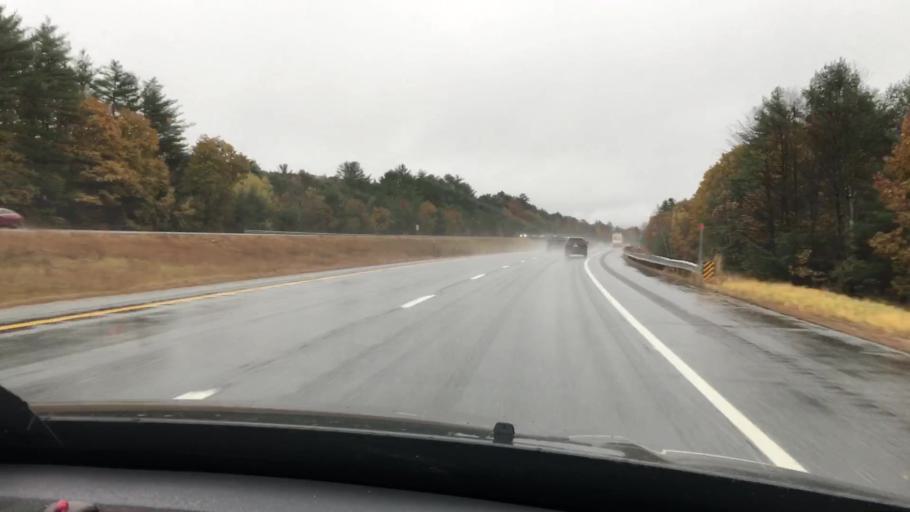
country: US
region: New Hampshire
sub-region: Grafton County
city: Ashland
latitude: 43.6447
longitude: -71.6475
